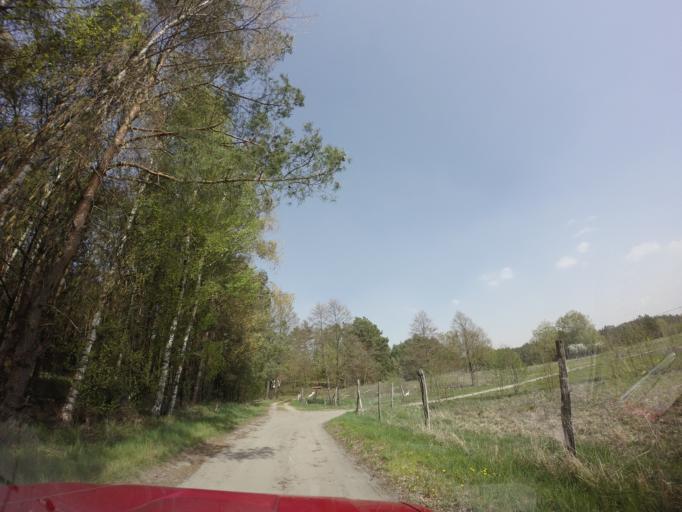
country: PL
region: West Pomeranian Voivodeship
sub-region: Powiat choszczenski
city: Drawno
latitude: 53.2344
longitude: 15.7563
